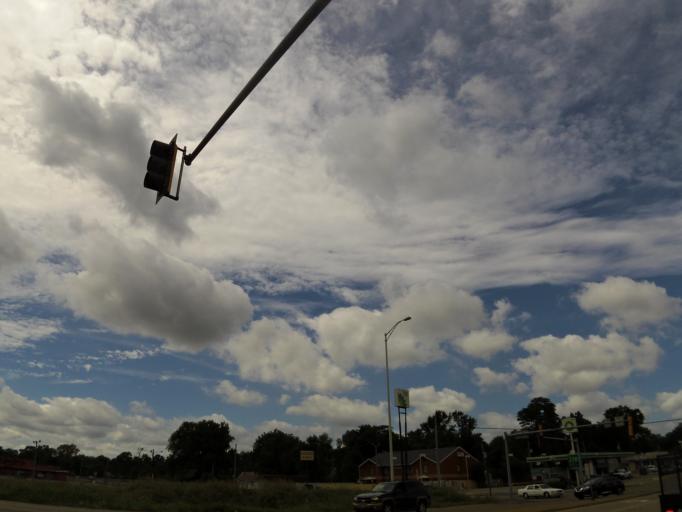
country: US
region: Illinois
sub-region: Saint Clair County
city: Washington Park
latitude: 38.6226
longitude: -90.0929
